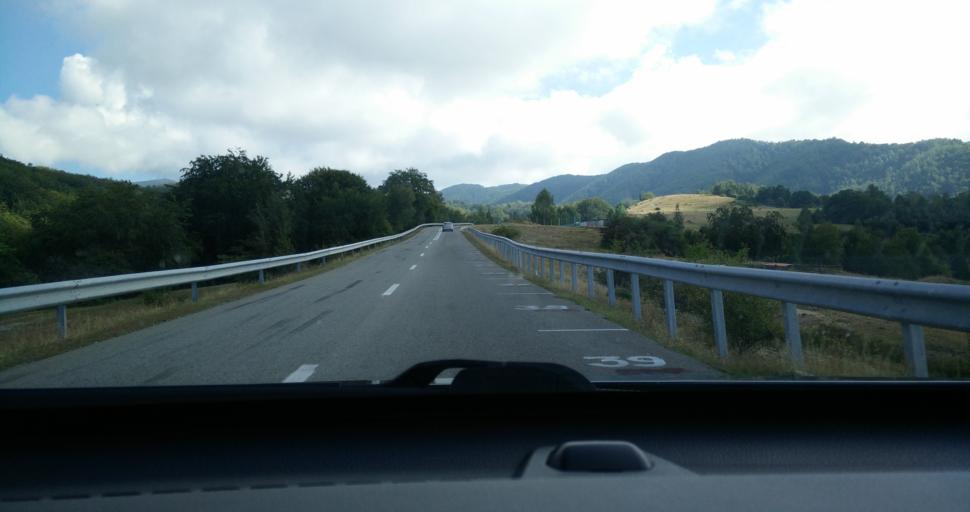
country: RO
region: Gorj
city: Novaci-Straini
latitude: 45.1979
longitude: 23.6891
